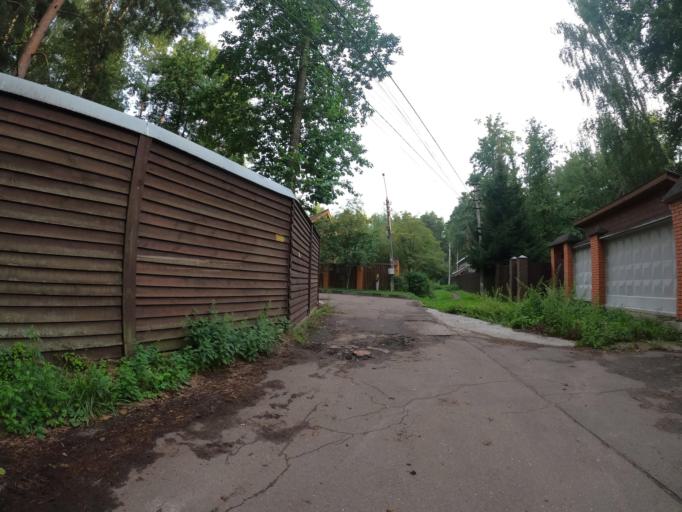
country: RU
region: Moskovskaya
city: Bykovo
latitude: 55.6363
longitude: 38.0947
